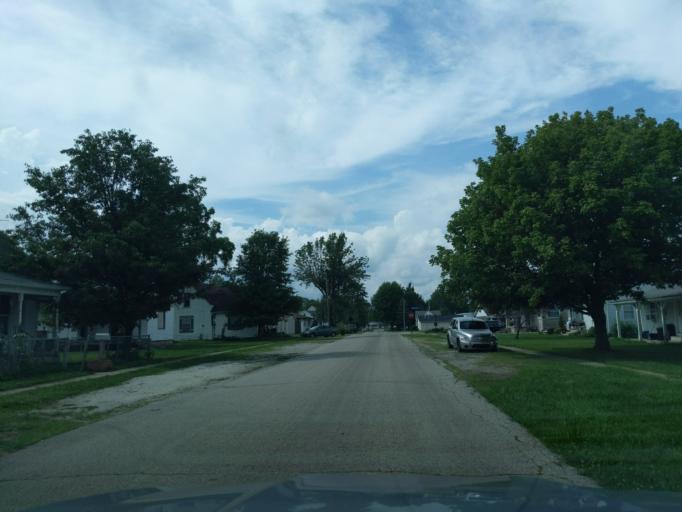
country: US
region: Indiana
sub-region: Ripley County
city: Osgood
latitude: 39.1300
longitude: -85.2940
